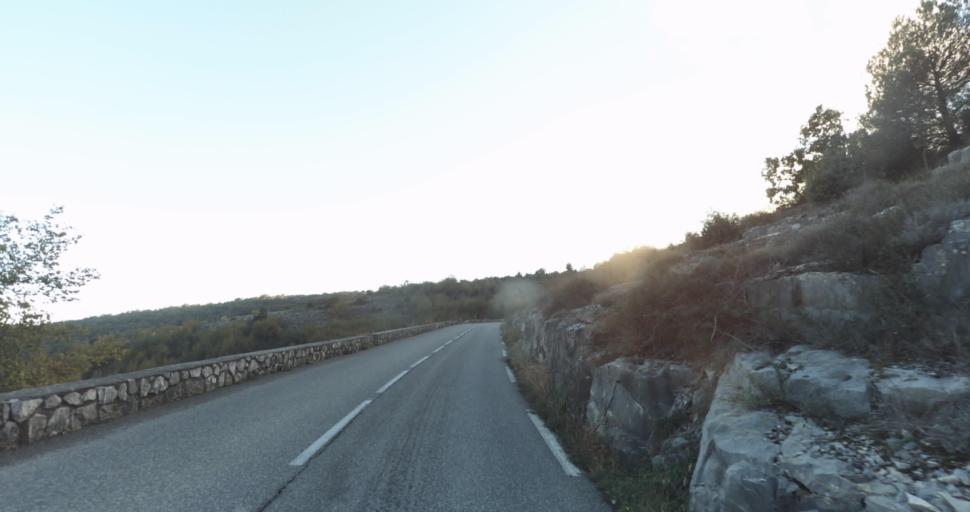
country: FR
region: Provence-Alpes-Cote d'Azur
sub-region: Departement des Alpes-Maritimes
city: Vence
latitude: 43.7533
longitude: 7.0932
